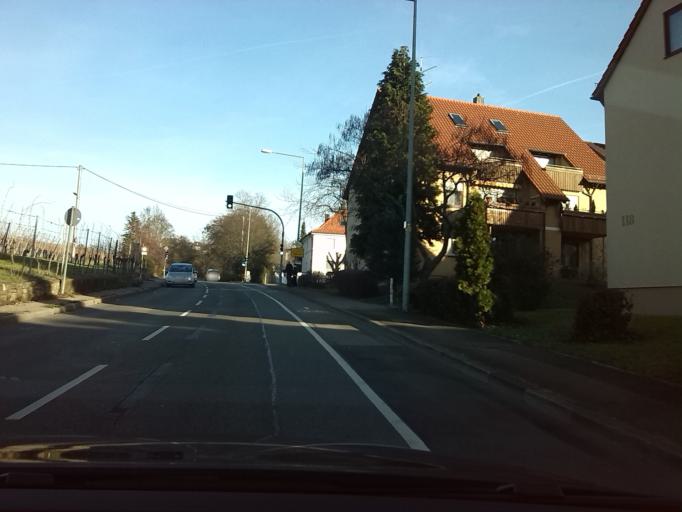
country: DE
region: Baden-Wuerttemberg
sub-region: Regierungsbezirk Stuttgart
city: Fellbach
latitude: 48.7949
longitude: 9.2570
